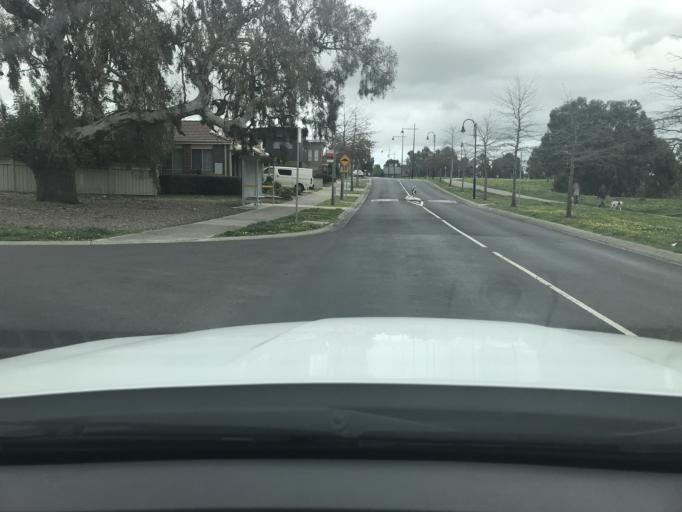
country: AU
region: Victoria
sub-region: Hume
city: Craigieburn
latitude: -37.5858
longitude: 144.9201
